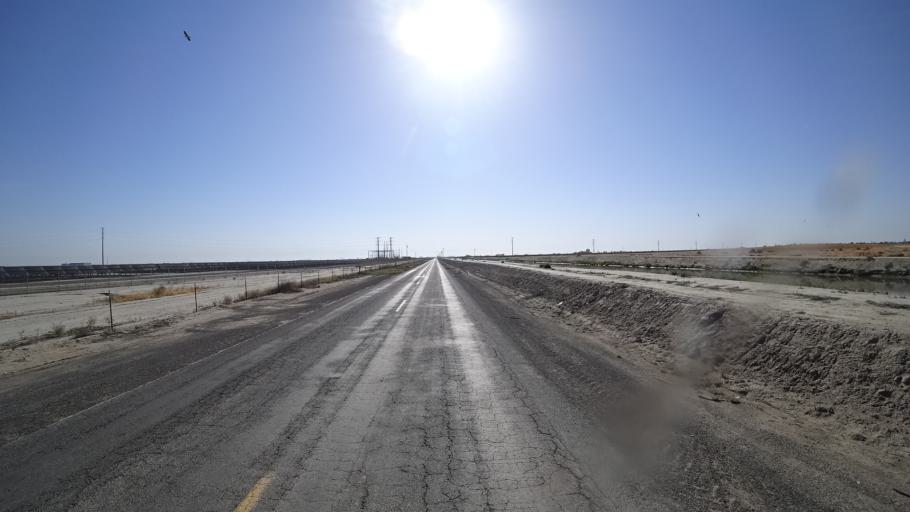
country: US
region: California
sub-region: Kings County
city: Corcoran
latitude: 36.1379
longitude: -119.5811
